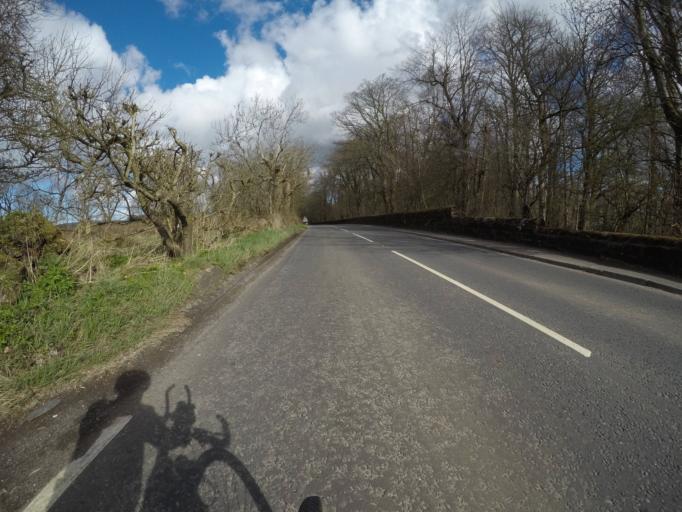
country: GB
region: Scotland
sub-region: North Ayrshire
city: Beith
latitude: 55.7429
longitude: -4.6256
